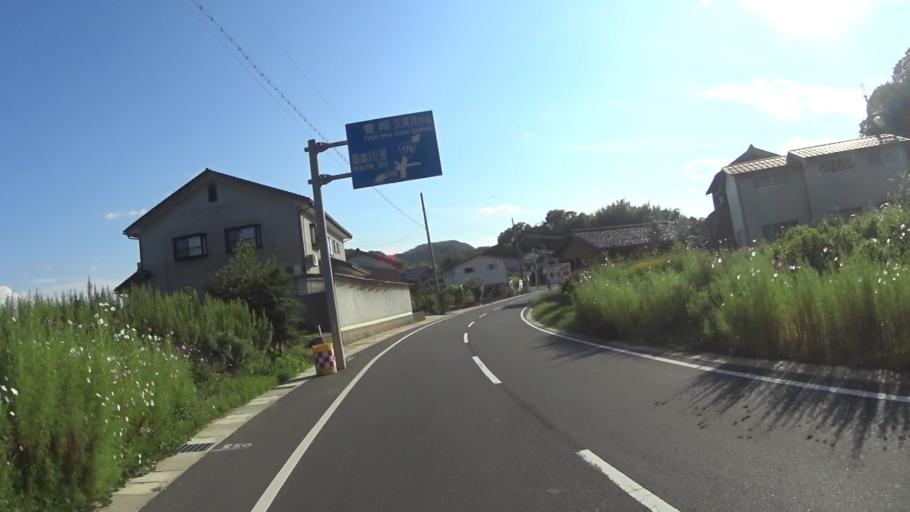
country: JP
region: Hyogo
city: Toyooka
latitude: 35.6369
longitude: 134.9420
